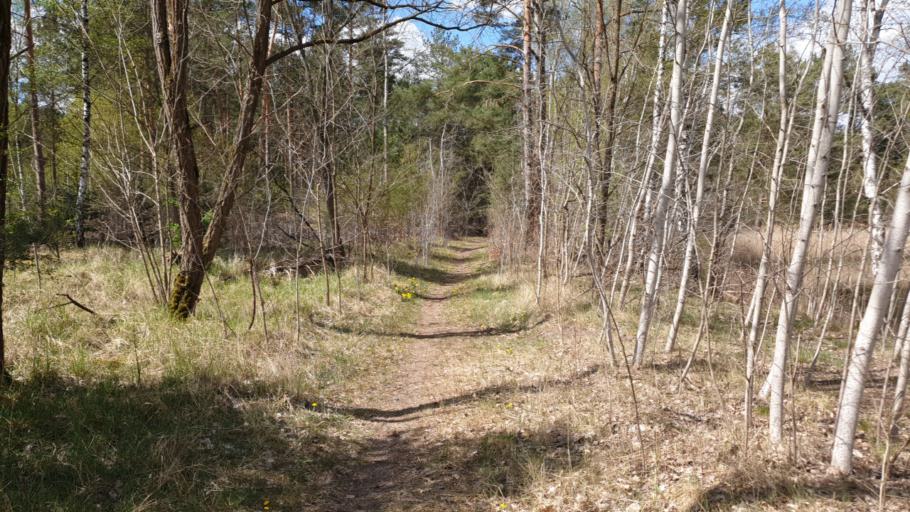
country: DE
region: Brandenburg
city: Teupitz
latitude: 52.0995
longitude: 13.6311
